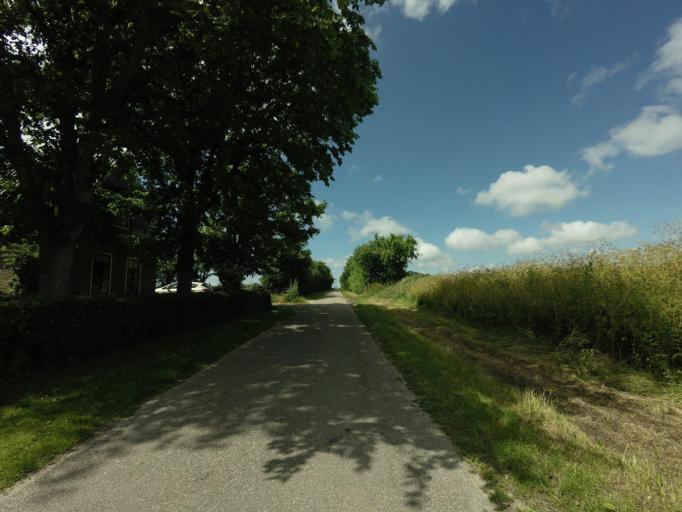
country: NL
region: North Holland
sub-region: Gemeente Texel
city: Den Burg
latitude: 53.0341
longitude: 4.8116
